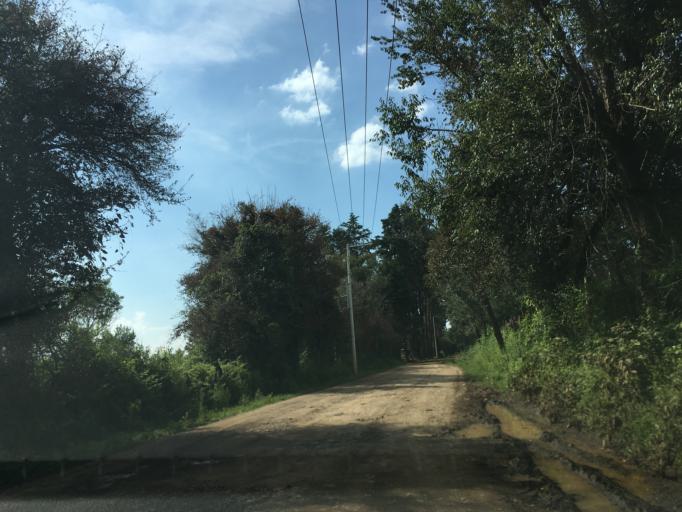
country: MX
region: Michoacan
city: Acuitzio del Canje
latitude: 19.5140
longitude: -101.2170
